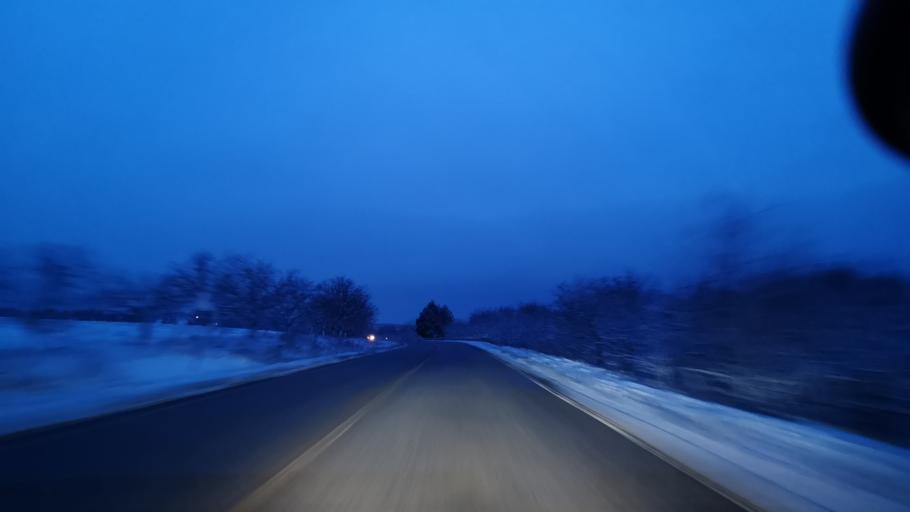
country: MD
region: Orhei
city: Orhei
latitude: 47.5542
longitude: 28.7951
